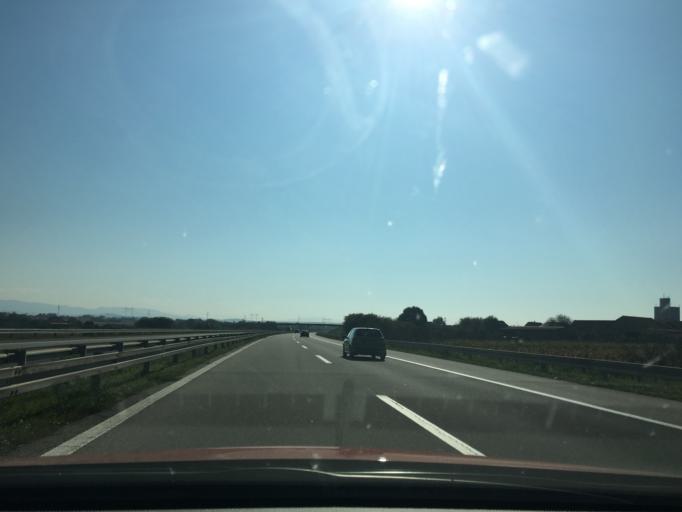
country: RS
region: Central Serbia
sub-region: Pomoravski Okrug
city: Cuprija
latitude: 43.9516
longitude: 21.3717
